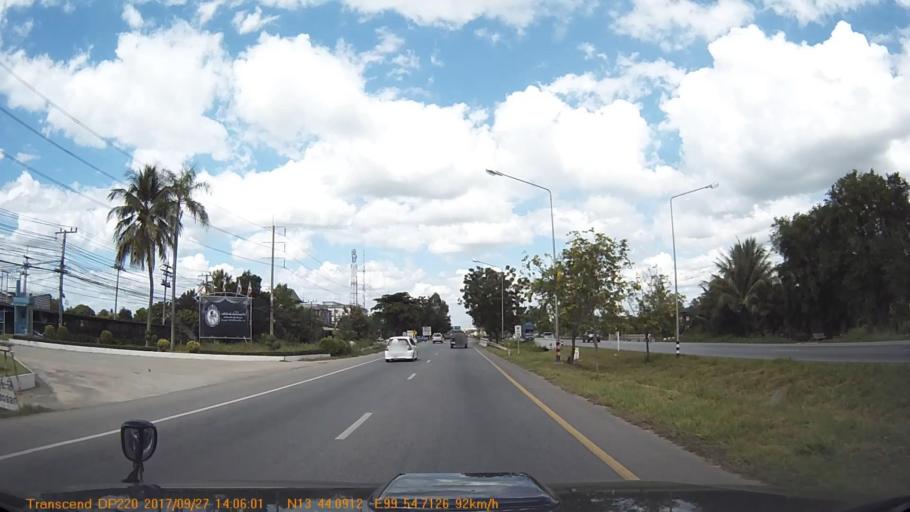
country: TH
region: Ratchaburi
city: Bang Phae
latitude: 13.7347
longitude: 99.9118
